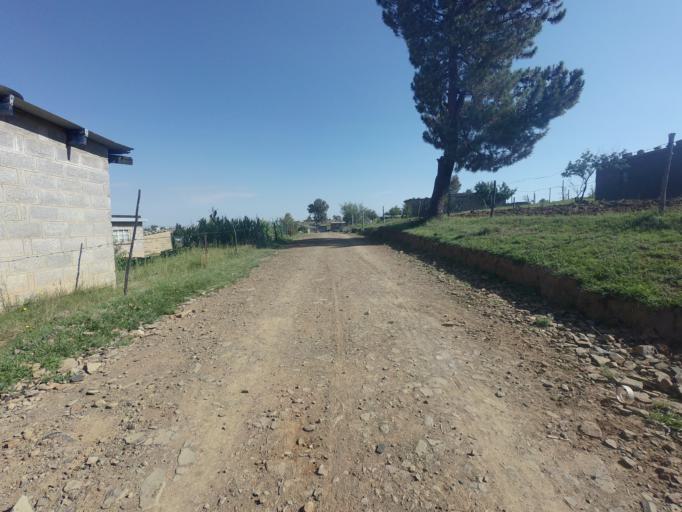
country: LS
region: Berea
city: Teyateyaneng
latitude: -29.1399
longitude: 27.7484
